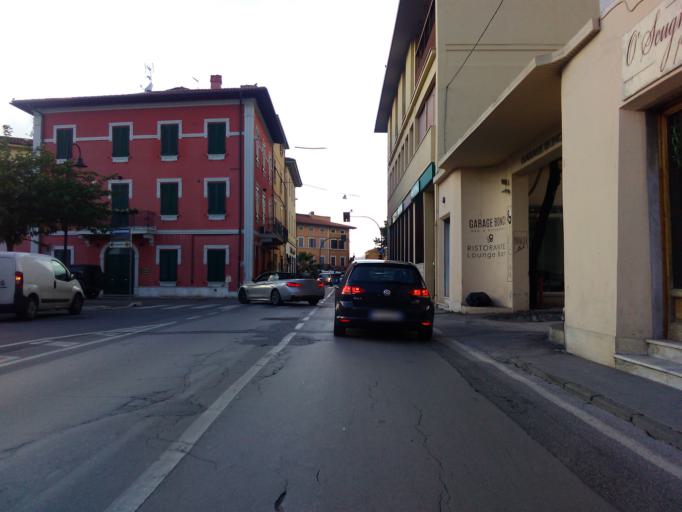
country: IT
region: Tuscany
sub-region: Provincia di Lucca
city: Pietrasanta
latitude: 43.9561
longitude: 10.2313
